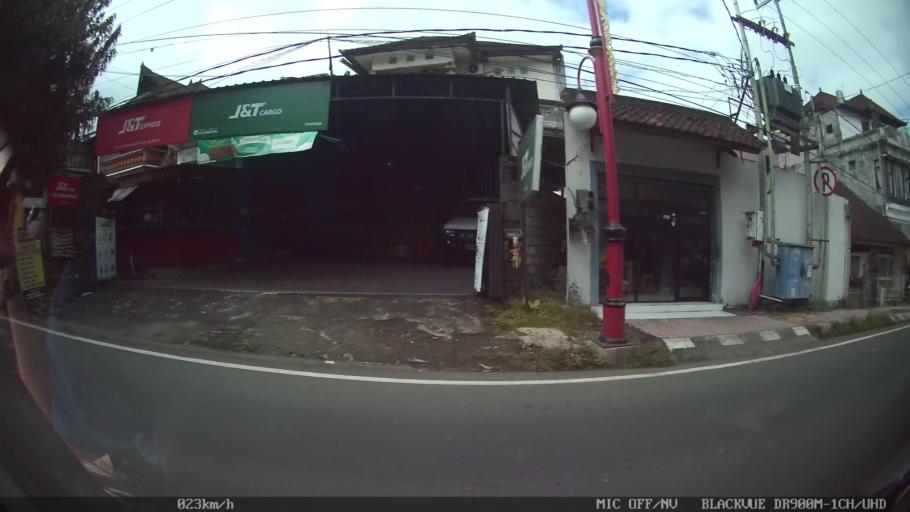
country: ID
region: Bali
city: Banjar Pesalakan
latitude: -8.5346
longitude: 115.3229
